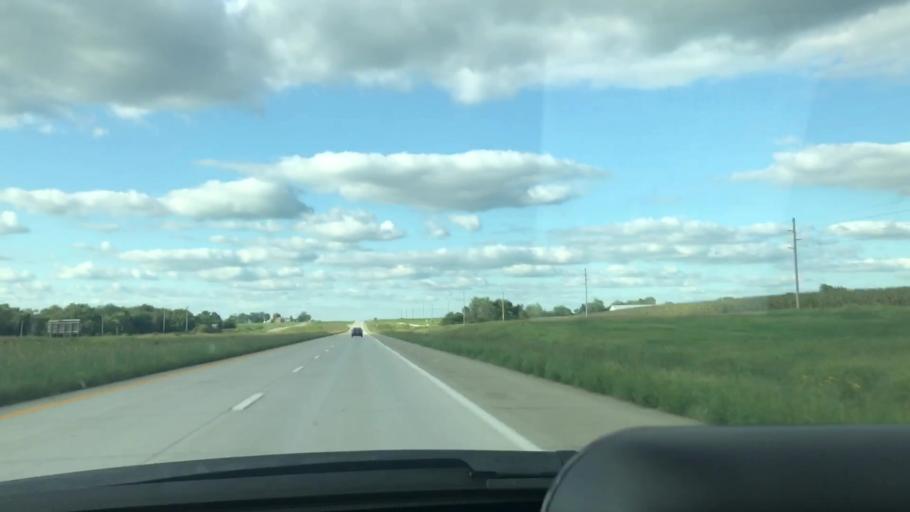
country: US
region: Missouri
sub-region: Benton County
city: Cole Camp
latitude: 38.4921
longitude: -93.2736
